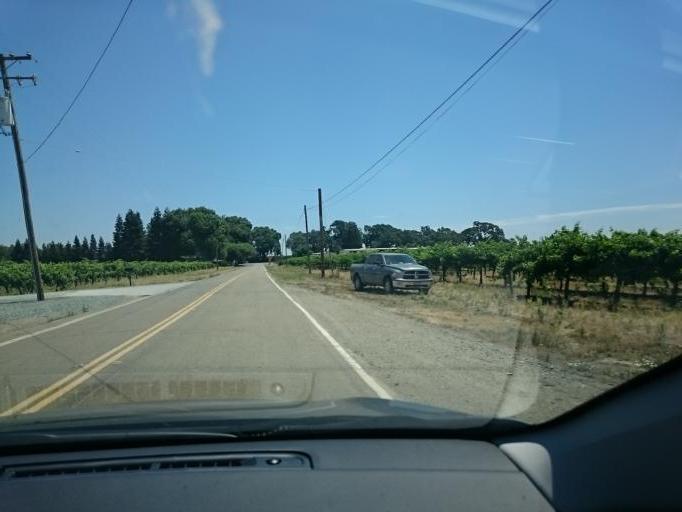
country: US
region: California
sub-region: San Joaquin County
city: Thornton
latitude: 38.2185
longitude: -121.4134
